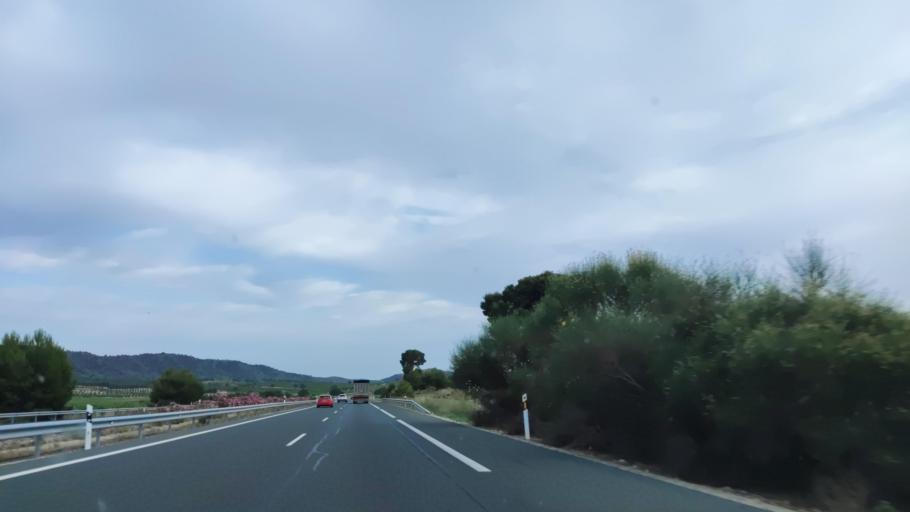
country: ES
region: Castille-La Mancha
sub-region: Provincia de Albacete
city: Tobarra
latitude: 38.6621
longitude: -1.6630
